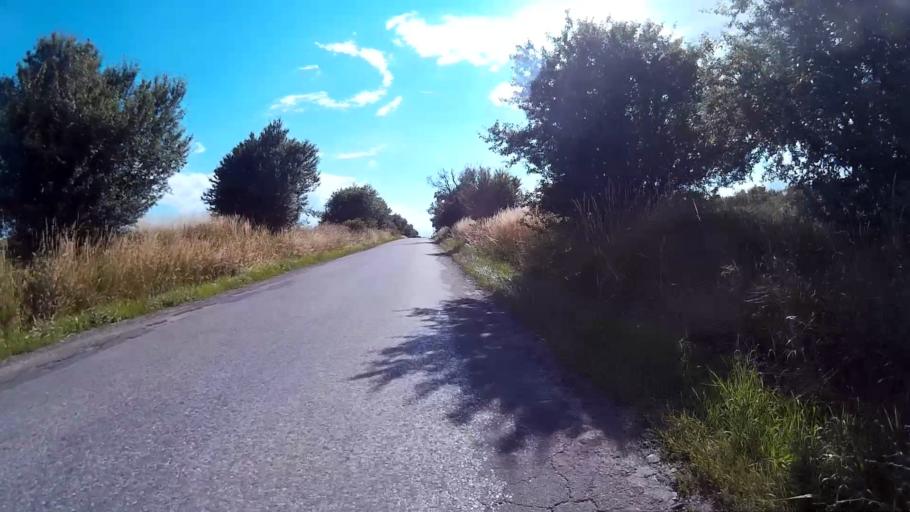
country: CZ
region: South Moravian
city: Troubsko
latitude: 49.1588
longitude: 16.5188
